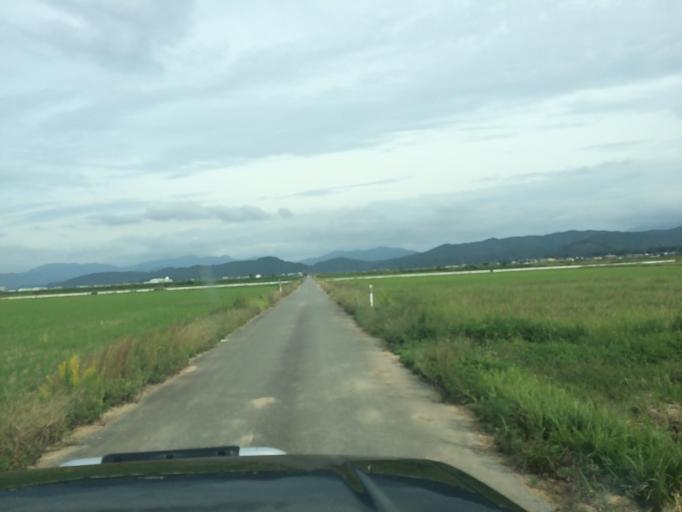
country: JP
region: Hyogo
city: Toyooka
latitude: 35.4871
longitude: 134.7810
